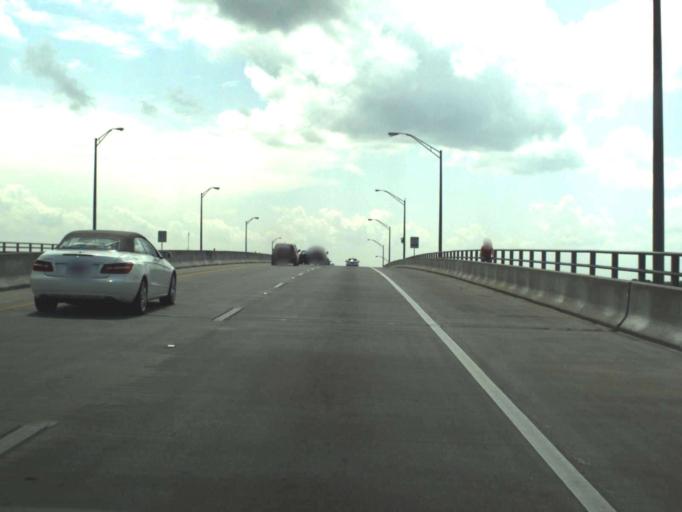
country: US
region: Florida
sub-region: Volusia County
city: New Smyrna Beach
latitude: 29.0242
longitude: -80.9166
